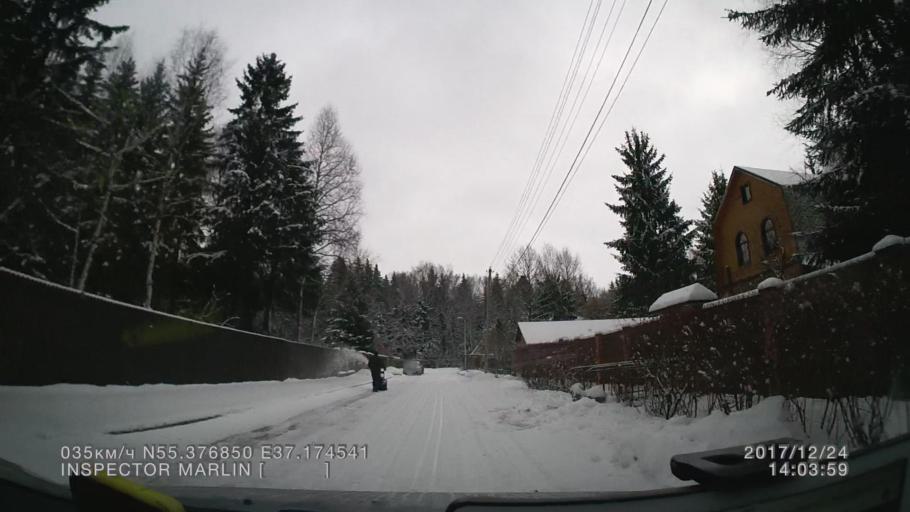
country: RU
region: Moskovskaya
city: Troitsk
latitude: 55.3768
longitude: 37.1747
